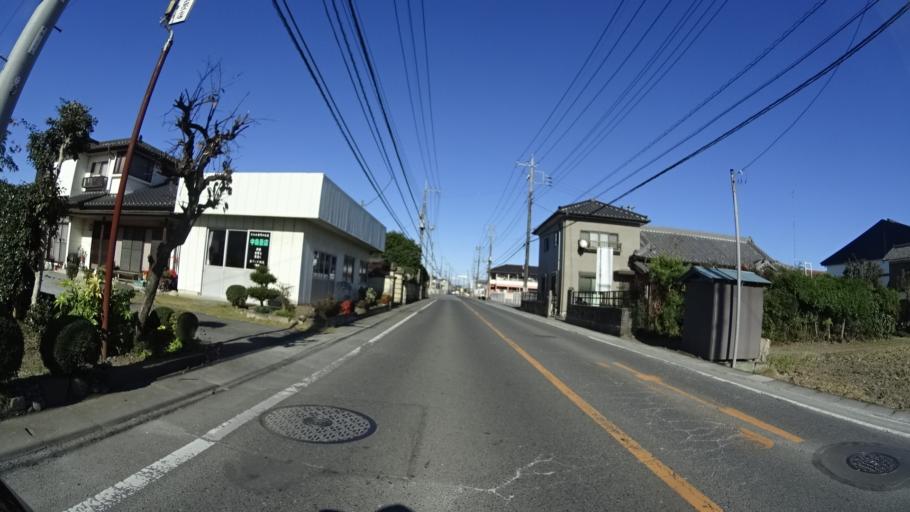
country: JP
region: Tochigi
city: Tochigi
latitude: 36.4086
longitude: 139.7447
